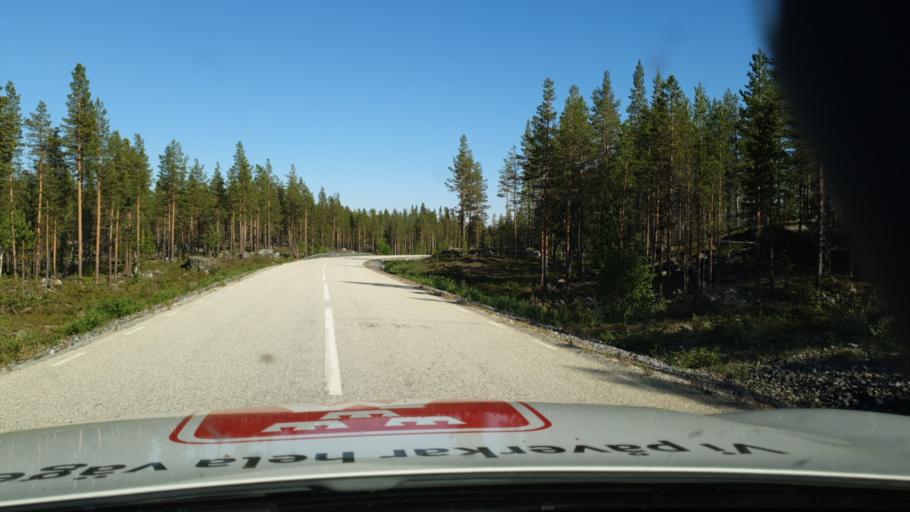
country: SE
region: Jaemtland
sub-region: Are Kommun
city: Jarpen
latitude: 62.8436
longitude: 13.4054
